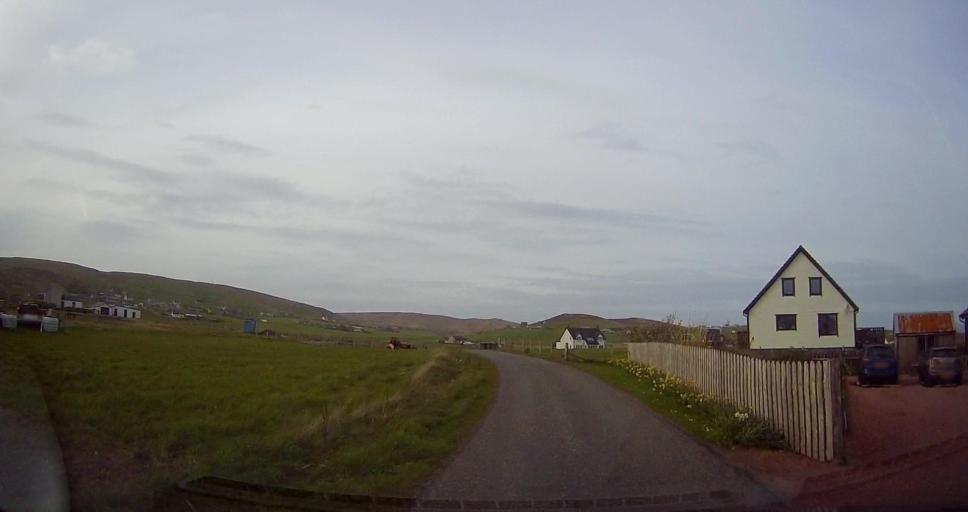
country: GB
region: Scotland
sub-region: Shetland Islands
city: Sandwick
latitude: 60.0395
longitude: -1.2183
